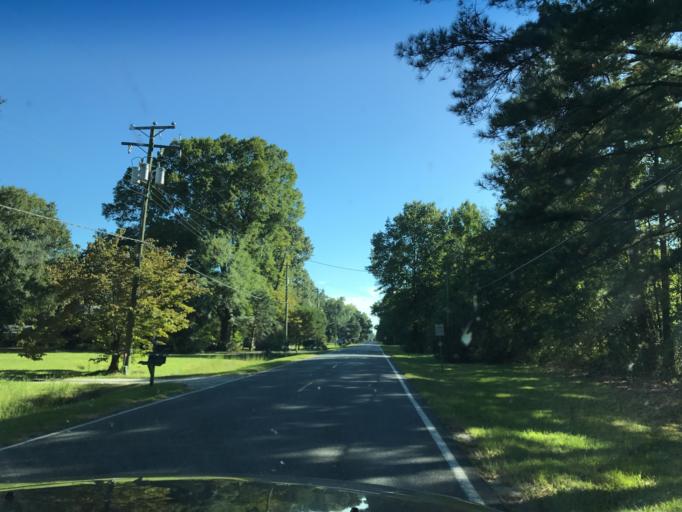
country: US
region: Virginia
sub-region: City of Portsmouth
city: Portsmouth Heights
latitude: 36.7351
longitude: -76.3461
